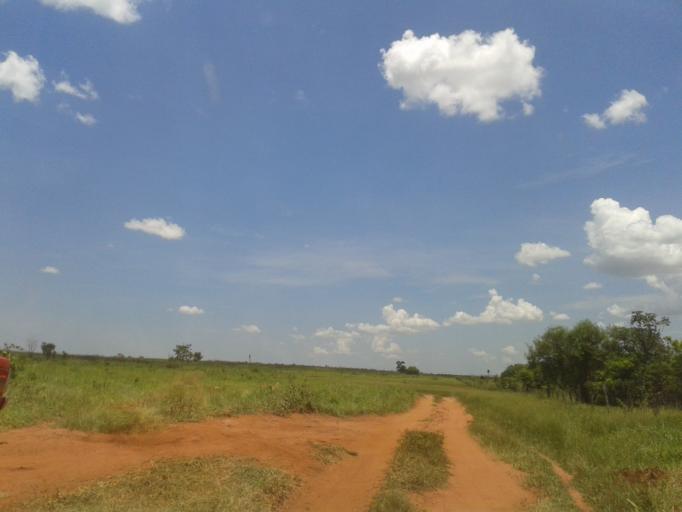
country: BR
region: Minas Gerais
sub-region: Santa Vitoria
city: Santa Vitoria
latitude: -19.2245
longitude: -50.4432
